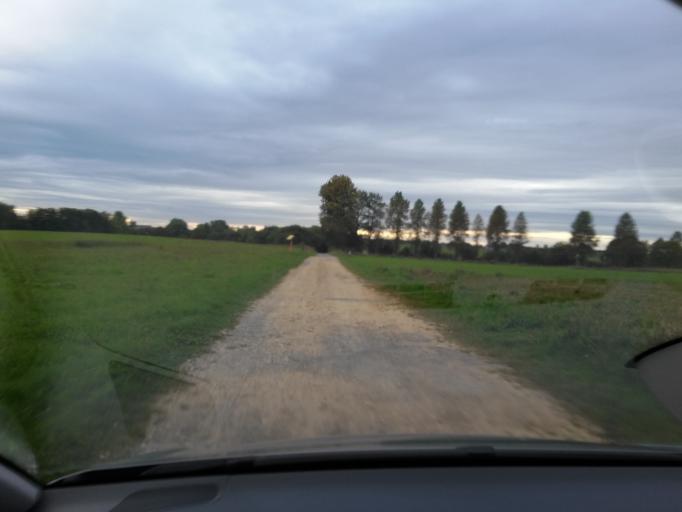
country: BE
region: Wallonia
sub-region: Province du Luxembourg
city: Etalle
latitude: 49.6773
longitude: 5.6301
